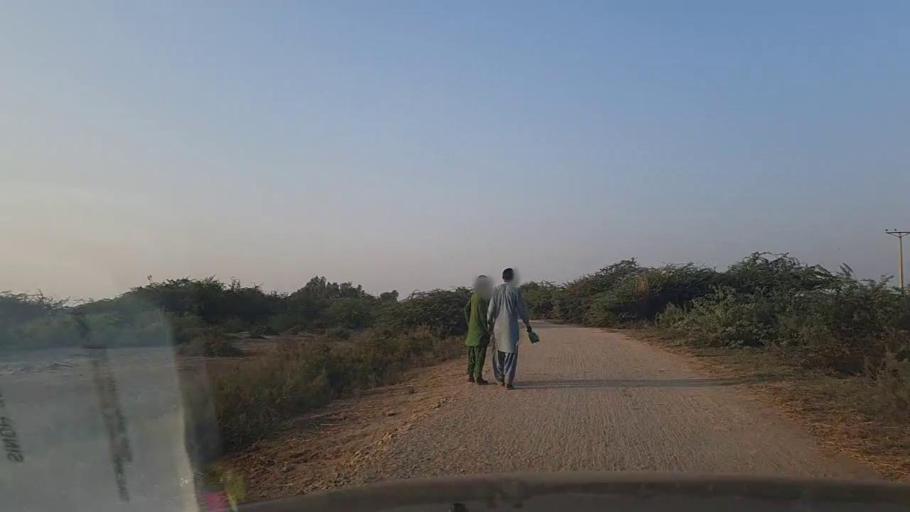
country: PK
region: Sindh
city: Keti Bandar
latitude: 24.3088
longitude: 67.6020
